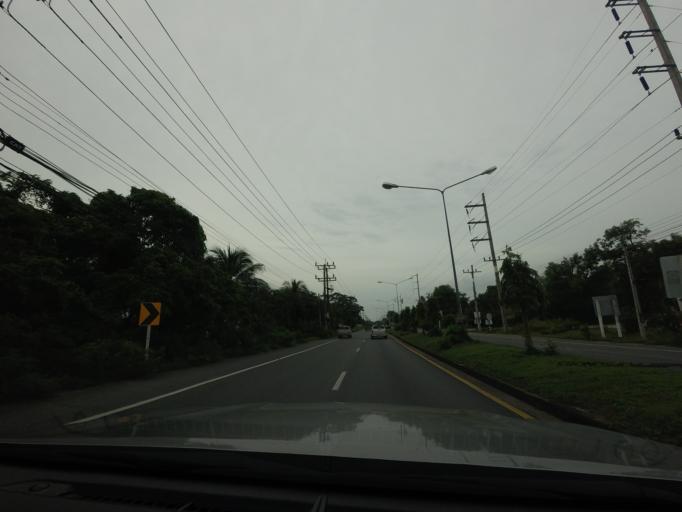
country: TH
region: Songkhla
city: Sathing Phra
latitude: 7.5532
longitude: 100.4142
